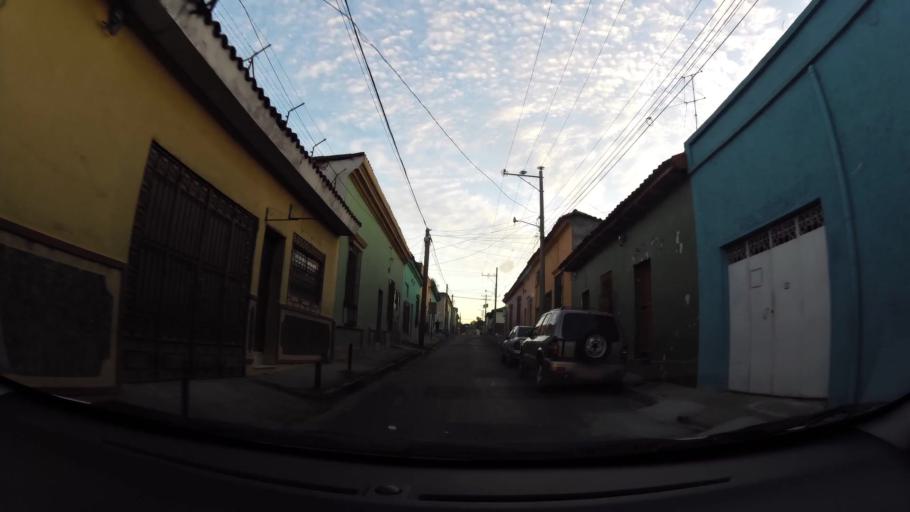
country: SV
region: Santa Ana
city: Santa Ana
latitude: 13.9922
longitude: -89.5537
